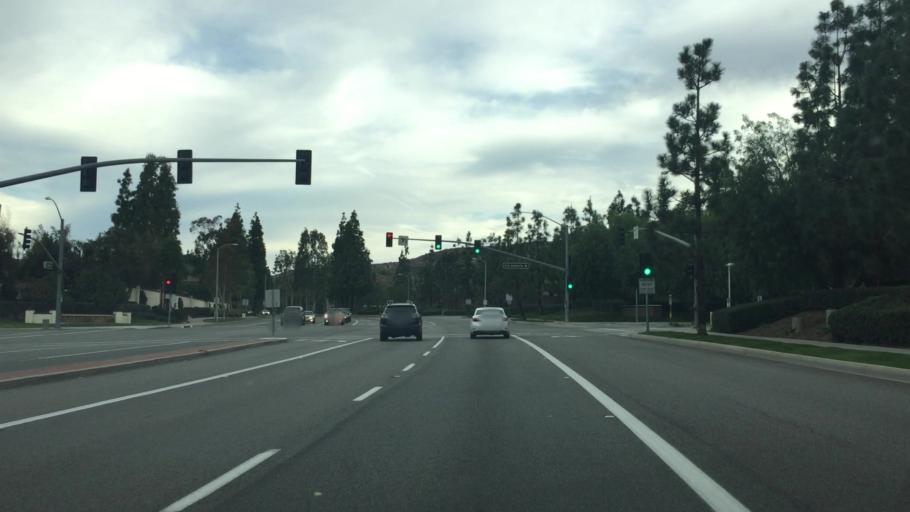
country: US
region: California
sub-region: Orange County
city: North Tustin
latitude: 33.7472
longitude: -117.7679
